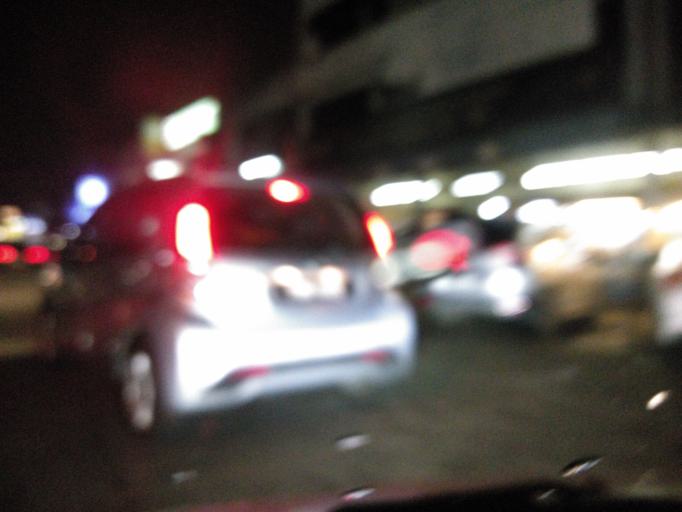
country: MY
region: Penang
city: Perai
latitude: 5.3850
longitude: 100.3930
